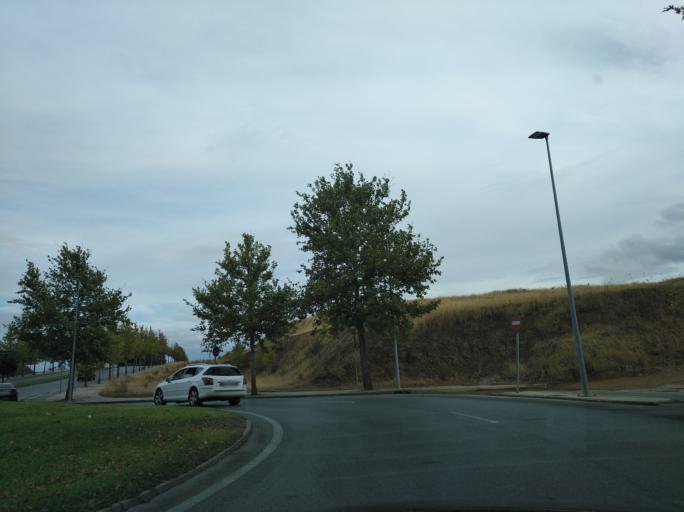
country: ES
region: Extremadura
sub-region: Provincia de Badajoz
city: Badajoz
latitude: 38.8641
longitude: -6.9770
